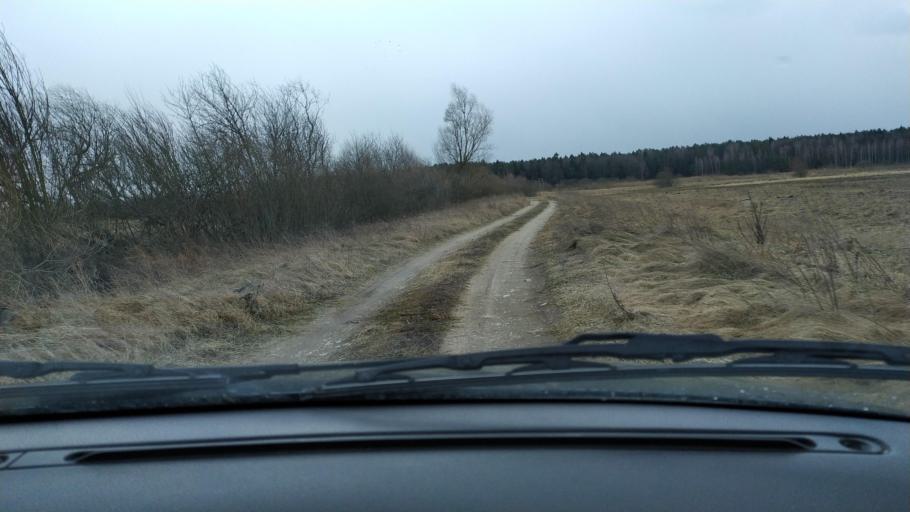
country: BY
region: Brest
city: Zhabinka
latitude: 52.4123
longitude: 24.0606
